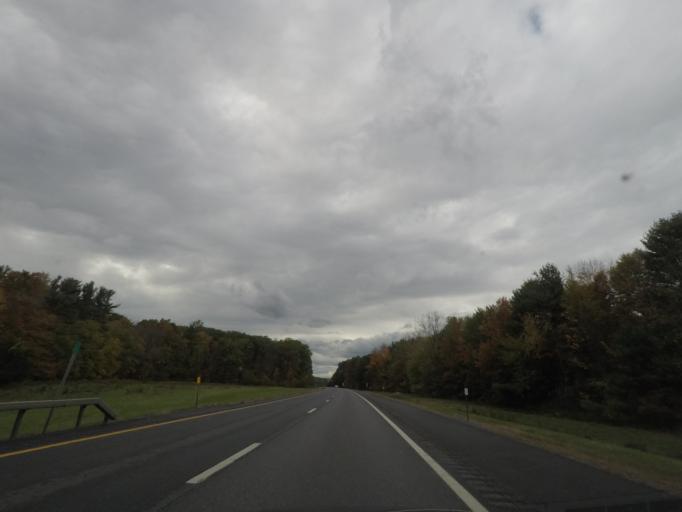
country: US
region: New York
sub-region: Rensselaer County
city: Castleton-on-Hudson
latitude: 42.4951
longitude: -73.7155
